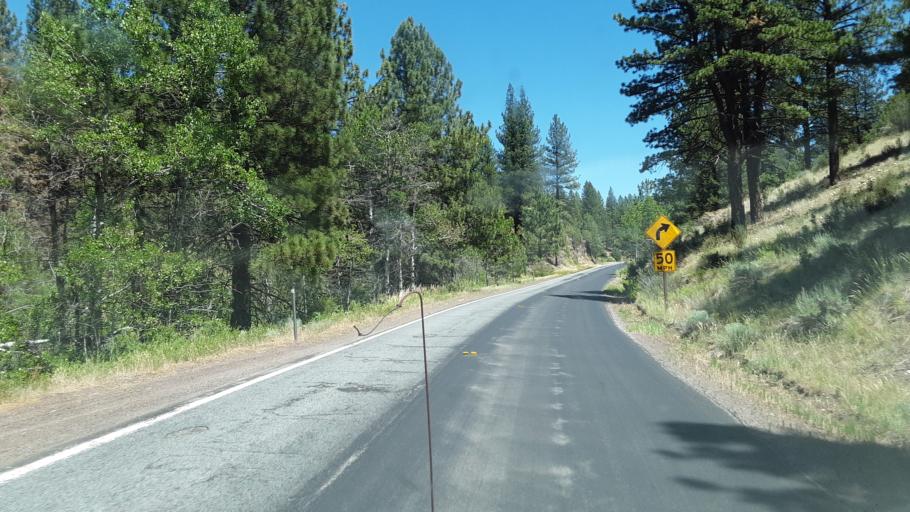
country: US
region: California
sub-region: Modoc County
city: Alturas
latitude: 41.0129
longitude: -120.8270
